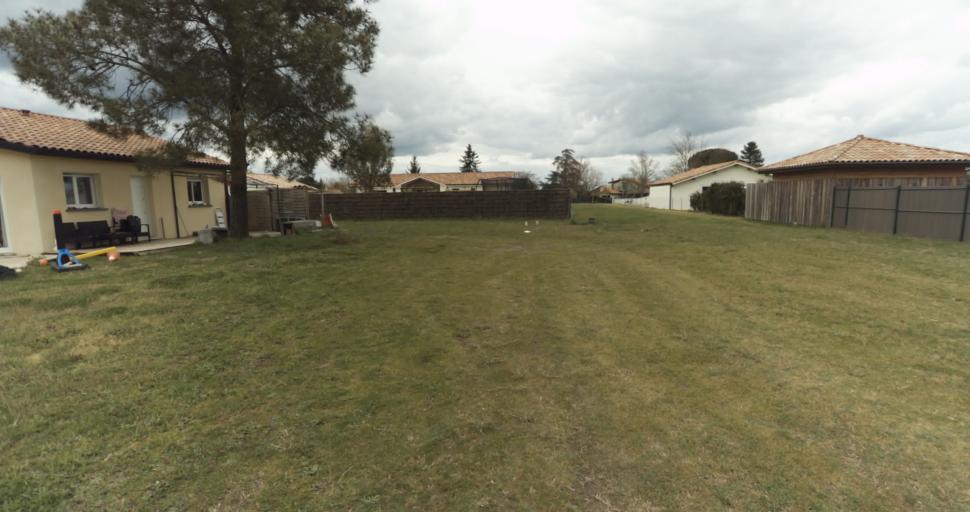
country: FR
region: Aquitaine
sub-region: Departement des Landes
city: Sarbazan
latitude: 44.0202
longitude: -0.3141
